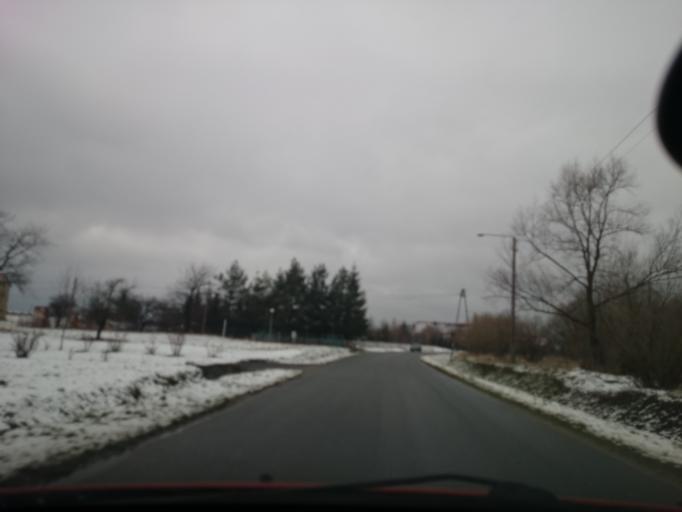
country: PL
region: Lower Silesian Voivodeship
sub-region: Powiat klodzki
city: Klodzko
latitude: 50.3808
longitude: 16.6653
